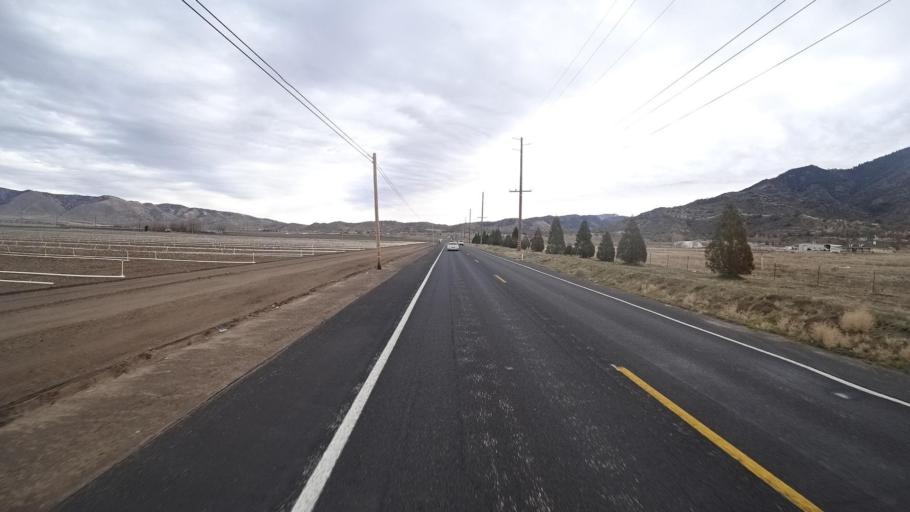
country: US
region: California
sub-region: Kern County
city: Stallion Springs
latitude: 35.0945
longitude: -118.6057
